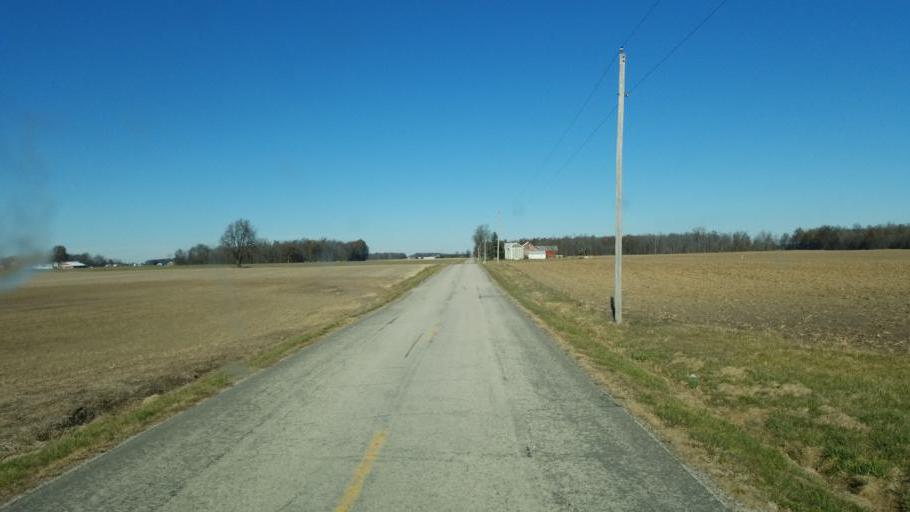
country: US
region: Ohio
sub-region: Crawford County
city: Crestline
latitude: 40.8997
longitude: -82.8264
